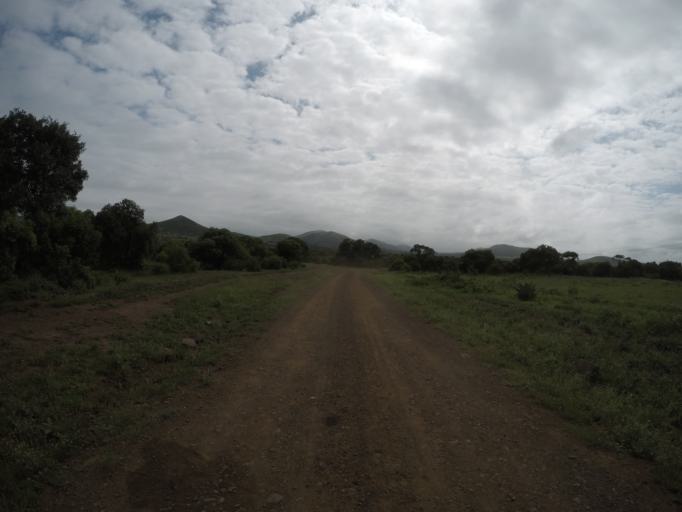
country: ZA
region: KwaZulu-Natal
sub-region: uThungulu District Municipality
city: Empangeni
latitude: -28.6231
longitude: 31.8554
